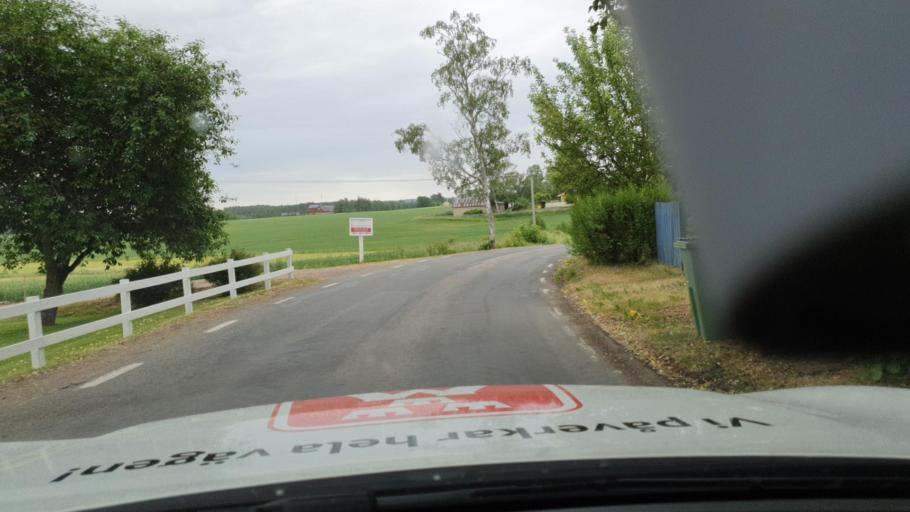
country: SE
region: Vaestra Goetaland
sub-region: Tidaholms Kommun
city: Olofstorp
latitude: 58.3370
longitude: 14.0488
